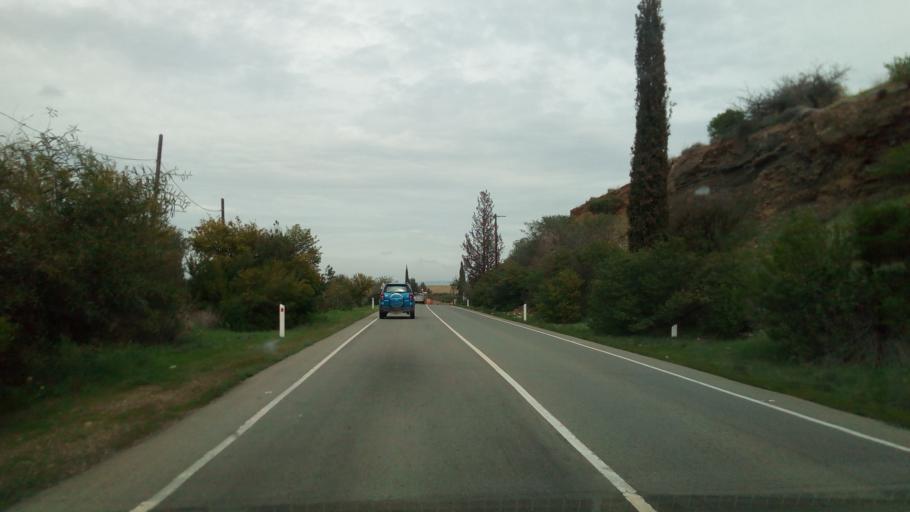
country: CY
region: Lefkosia
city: Astromeritis
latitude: 35.1017
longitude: 32.9712
